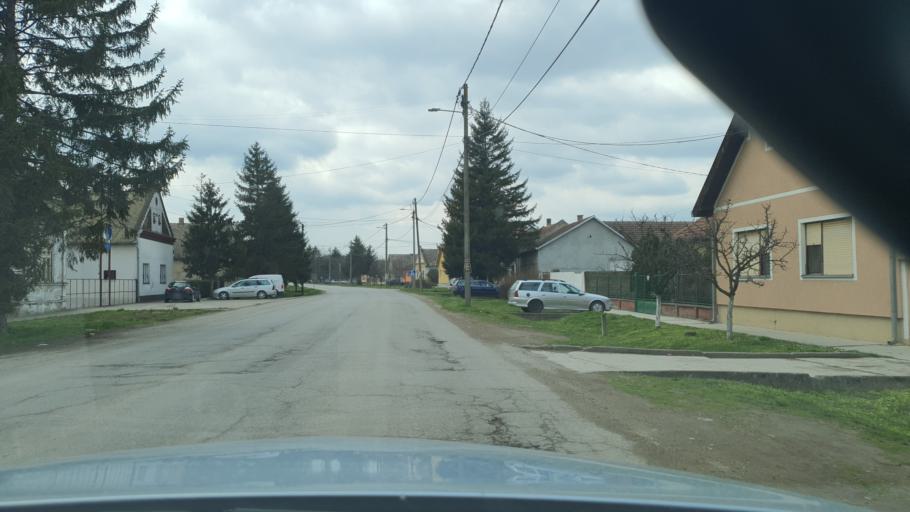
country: RS
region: Autonomna Pokrajina Vojvodina
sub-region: Juznobacki Okrug
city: Bac
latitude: 45.3961
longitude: 19.2423
